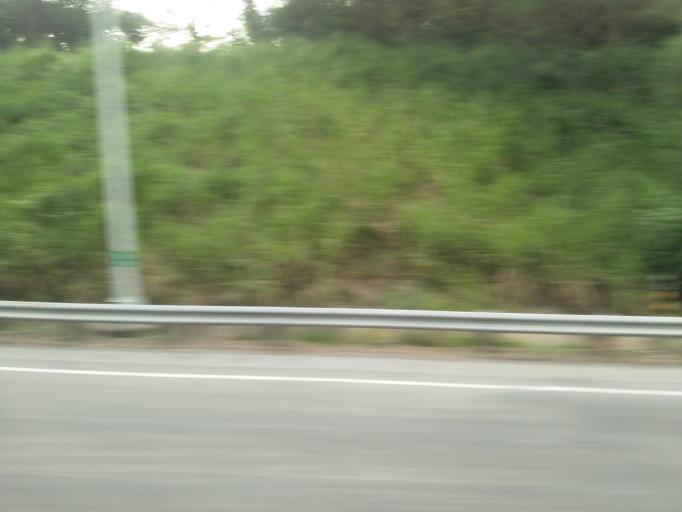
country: TW
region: Taiwan
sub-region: Pingtung
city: Pingtung
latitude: 22.7891
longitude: 120.4288
